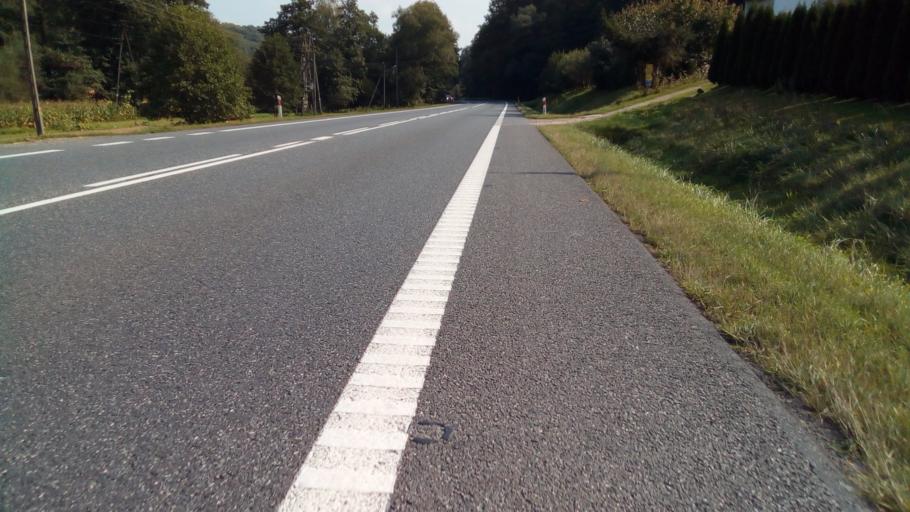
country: PL
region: Subcarpathian Voivodeship
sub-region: Powiat strzyzowski
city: Jawornik
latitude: 49.8161
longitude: 21.8766
